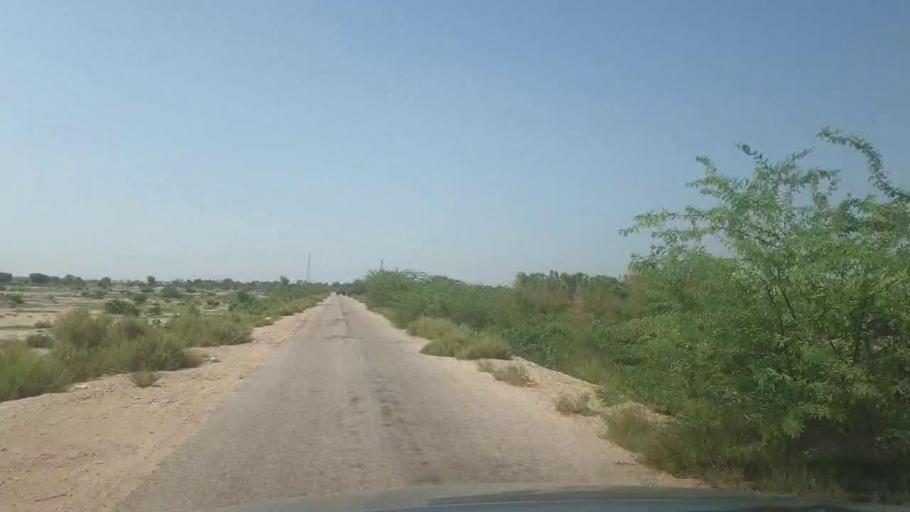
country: PK
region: Sindh
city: Rohri
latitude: 27.4162
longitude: 69.0801
